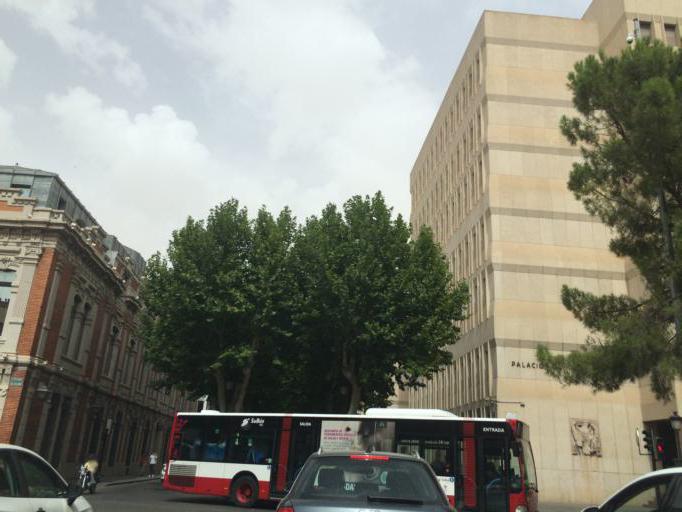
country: ES
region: Castille-La Mancha
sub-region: Provincia de Albacete
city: Albacete
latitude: 38.9947
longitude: -1.8538
